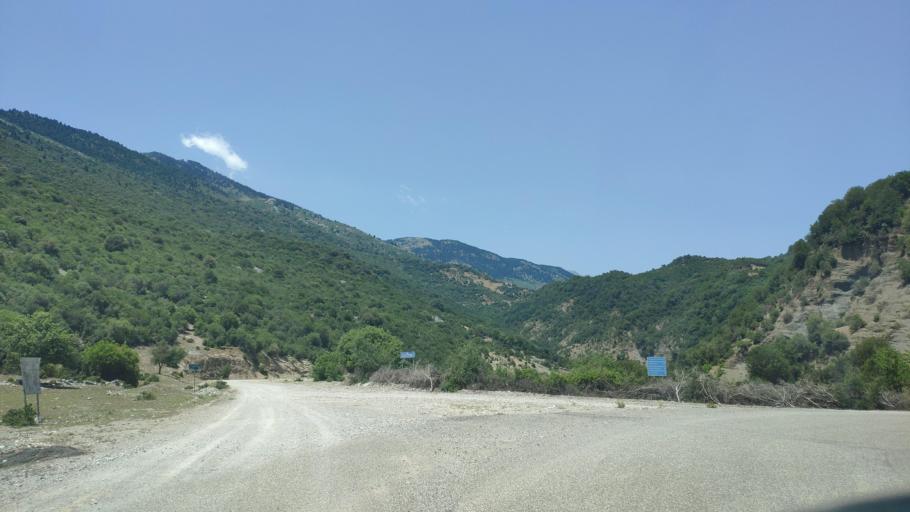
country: GR
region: Thessaly
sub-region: Nomos Kardhitsas
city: Anthiro
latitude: 39.1645
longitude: 21.3756
